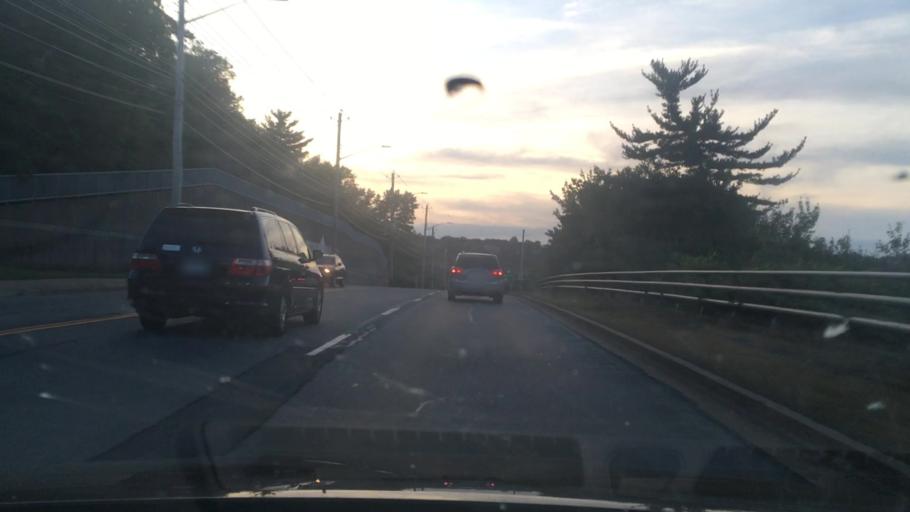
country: CA
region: Nova Scotia
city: Dartmouth
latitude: 44.6805
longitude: -63.6566
